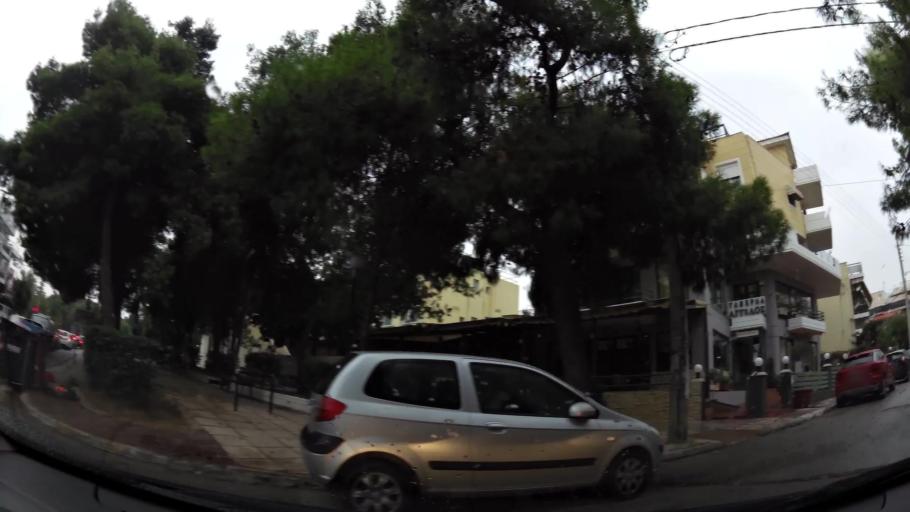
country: GR
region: Attica
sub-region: Nomarchia Athinas
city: Chaidari
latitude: 38.0011
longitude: 23.6630
